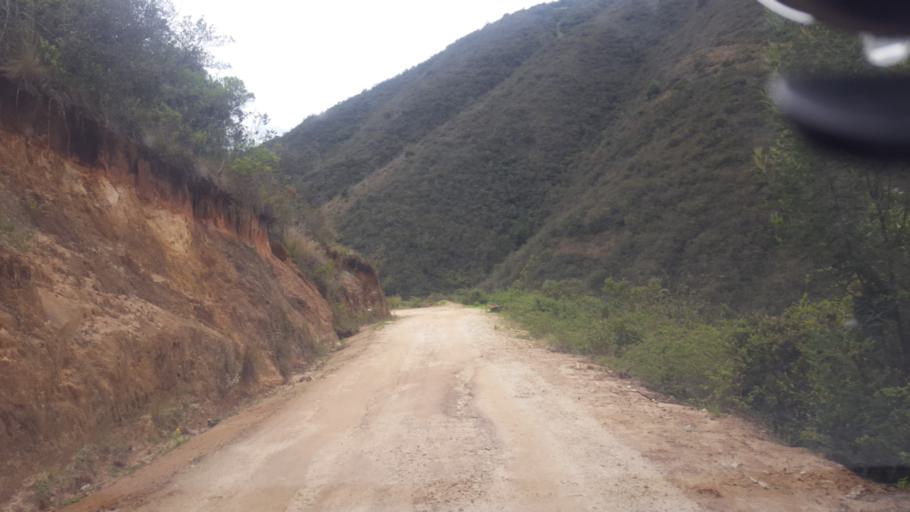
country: CO
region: Boyaca
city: Belen
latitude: 6.0141
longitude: -72.8779
